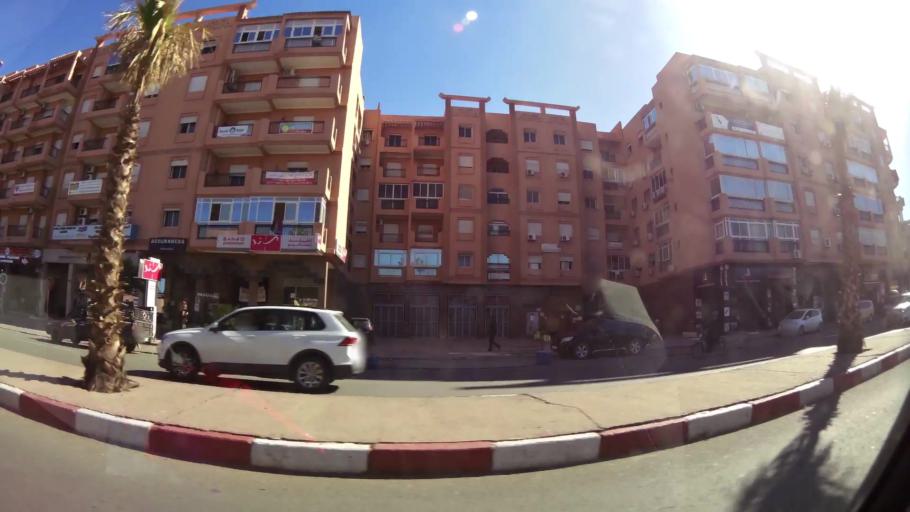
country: MA
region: Marrakech-Tensift-Al Haouz
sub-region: Marrakech
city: Marrakesh
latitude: 31.6370
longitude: -8.0019
